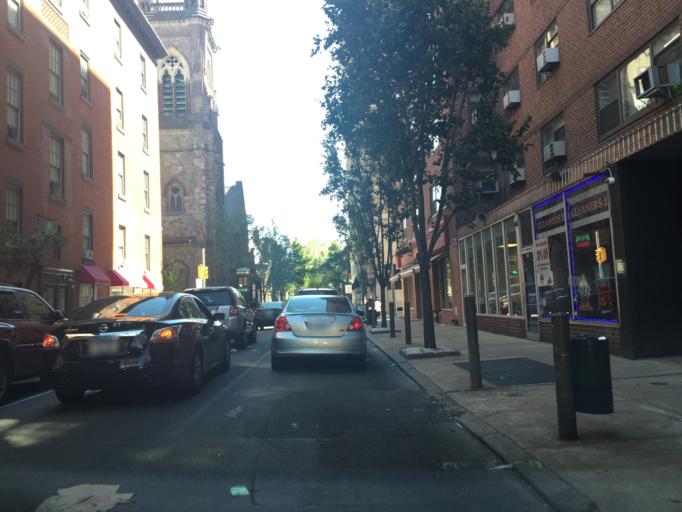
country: US
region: Pennsylvania
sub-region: Philadelphia County
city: Philadelphia
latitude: 39.9512
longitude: -75.1756
